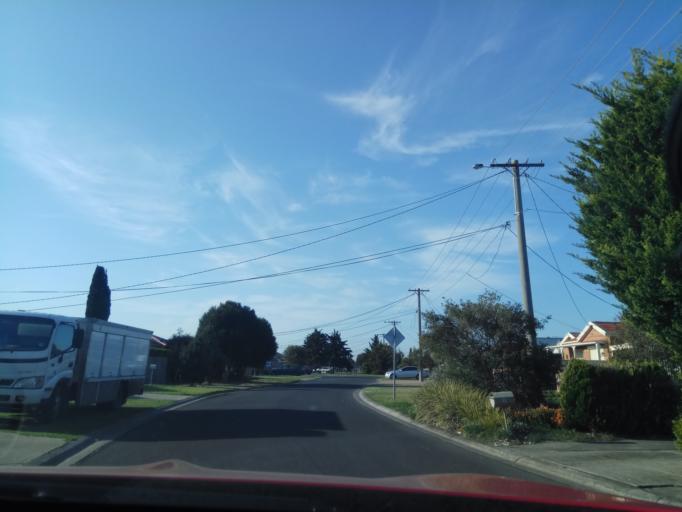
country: AU
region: Victoria
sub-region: Hobsons Bay
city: Laverton
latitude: -37.8761
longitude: 144.7701
